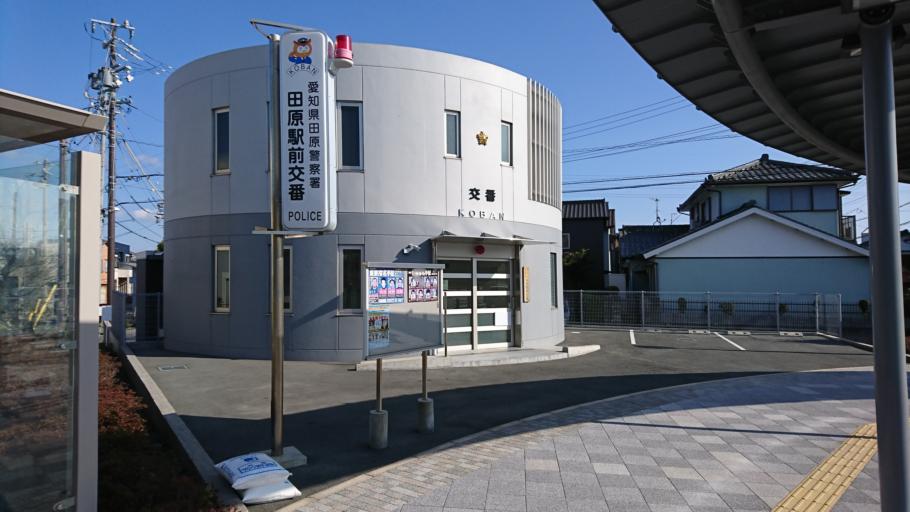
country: JP
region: Aichi
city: Tahara
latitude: 34.6666
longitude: 137.2688
